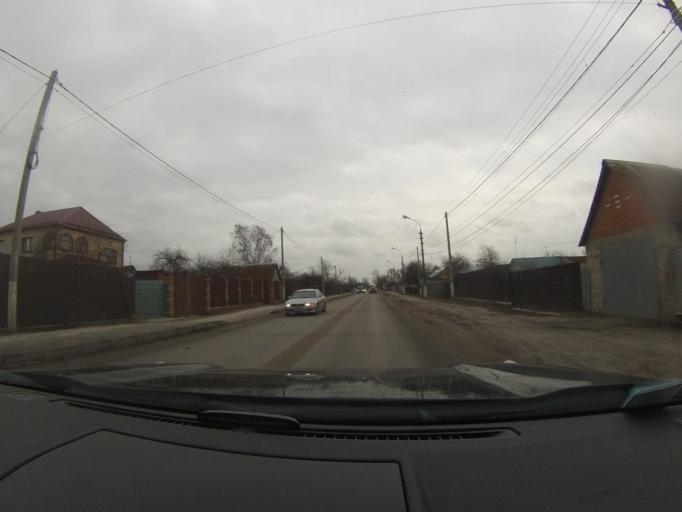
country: RU
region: Moskovskaya
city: Lopatinskiy
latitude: 55.3293
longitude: 38.7119
